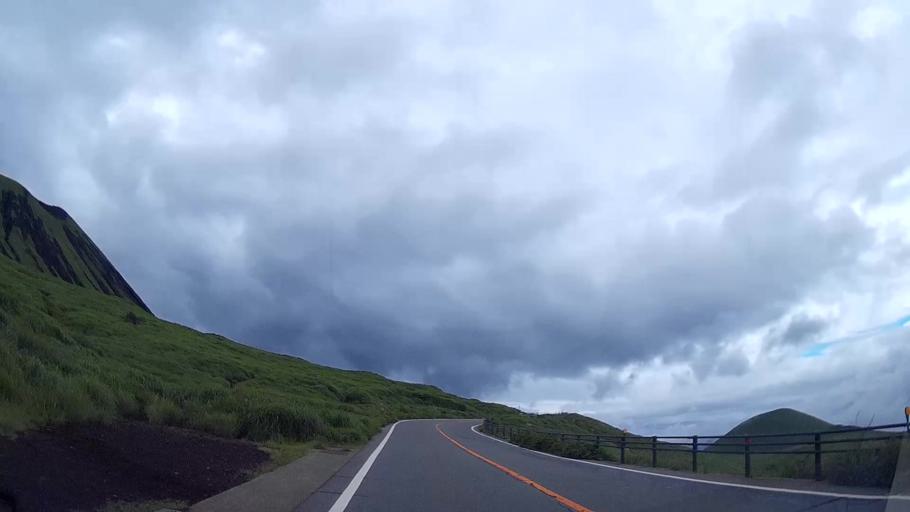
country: JP
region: Kumamoto
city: Aso
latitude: 32.9061
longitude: 131.0568
